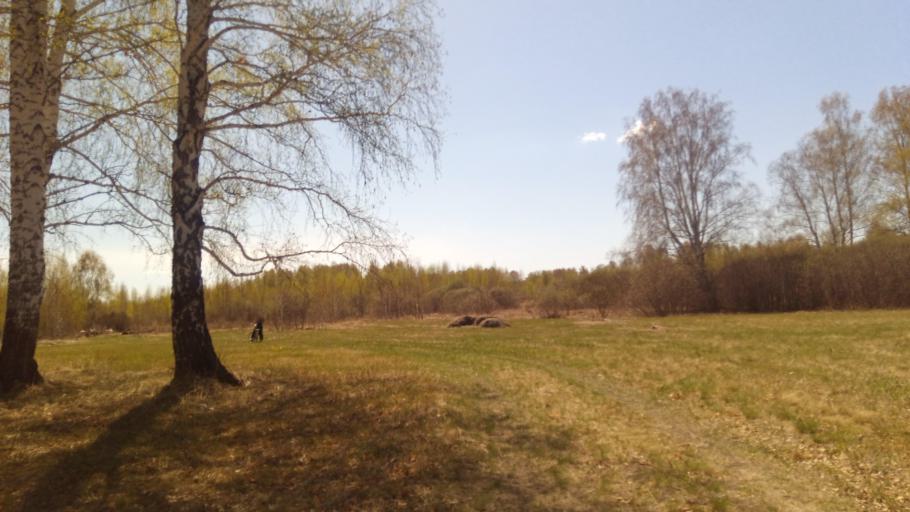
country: RU
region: Chelyabinsk
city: Timiryazevskiy
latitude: 54.9983
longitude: 60.8506
